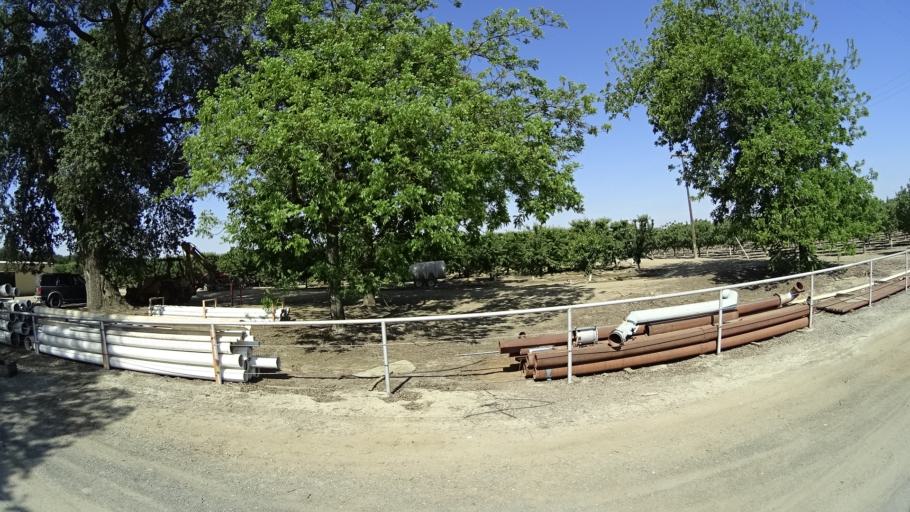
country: US
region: California
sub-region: Kings County
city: Lemoore
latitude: 36.3401
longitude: -119.8430
